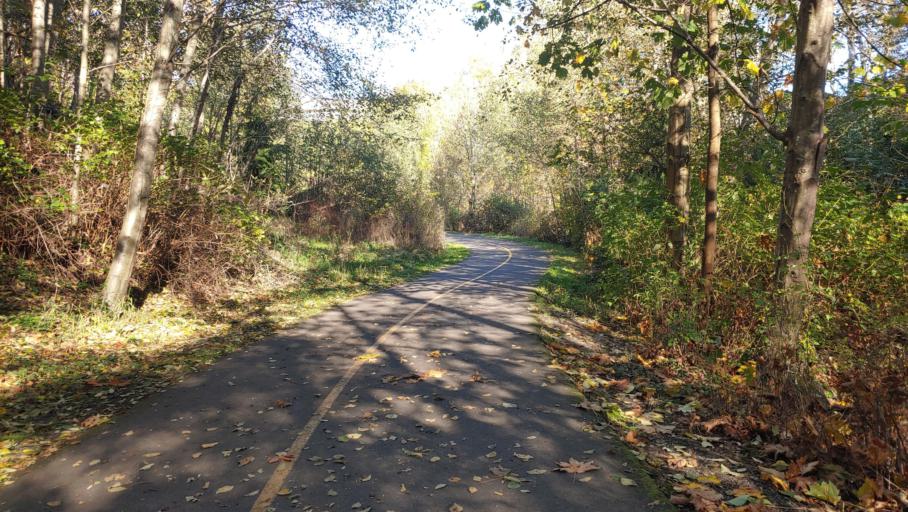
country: US
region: Washington
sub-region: King County
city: Des Moines
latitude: 47.4074
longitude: -122.3268
